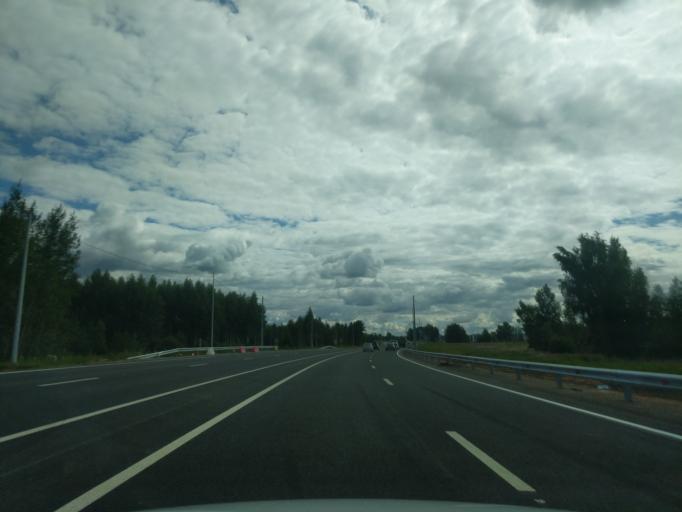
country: RU
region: Kostroma
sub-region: Kostromskoy Rayon
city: Kostroma
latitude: 57.7375
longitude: 40.8662
